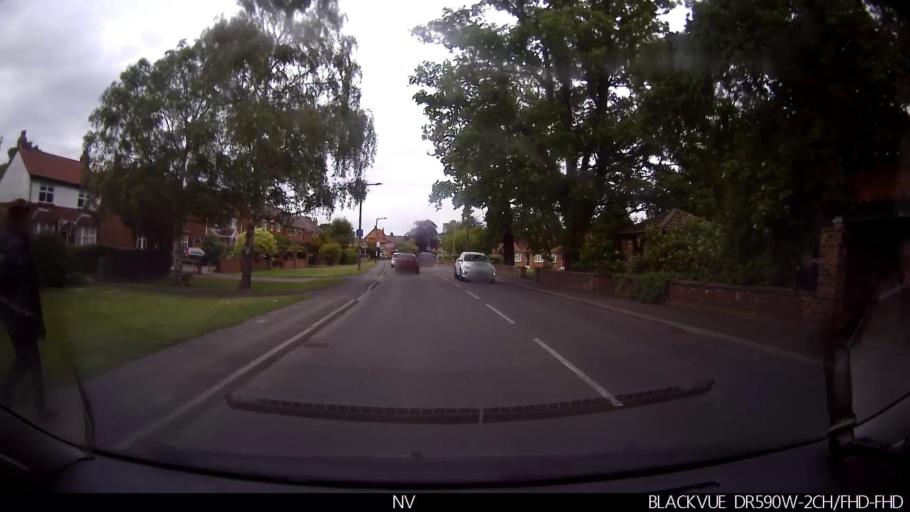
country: GB
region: England
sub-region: City of York
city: Haxby
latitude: 54.0131
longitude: -1.0726
